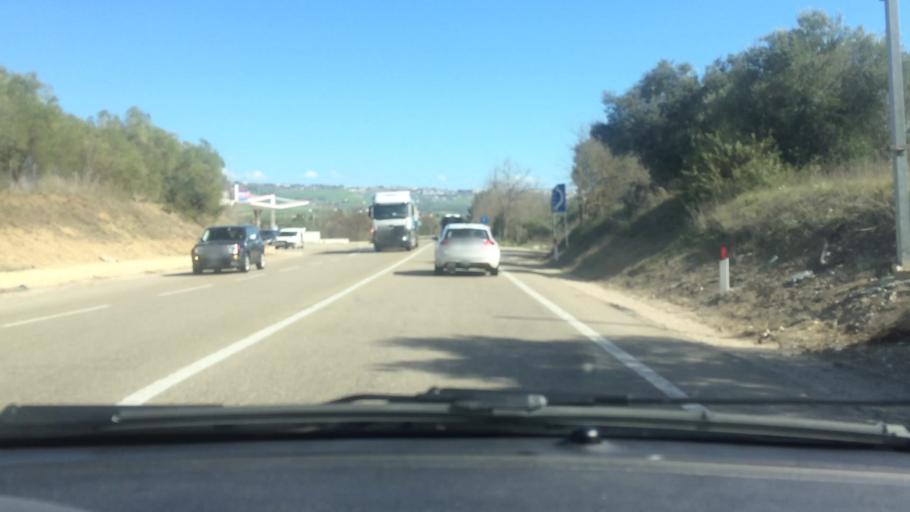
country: IT
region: Basilicate
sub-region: Provincia di Matera
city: La Martella
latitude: 40.6059
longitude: 16.5694
